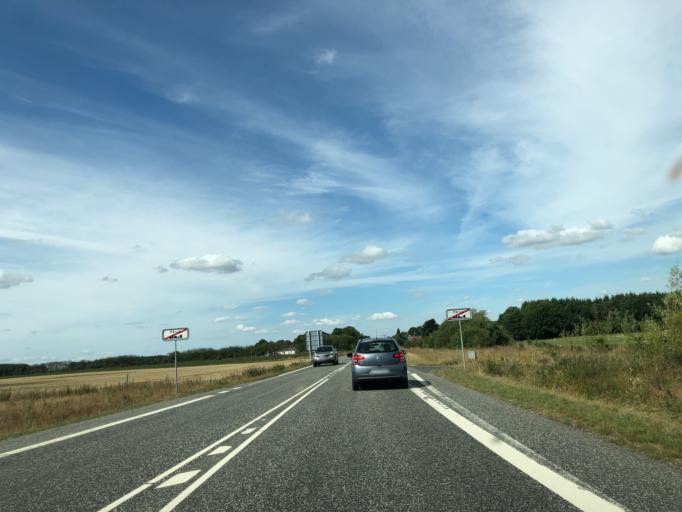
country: DK
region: Central Jutland
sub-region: Ikast-Brande Kommune
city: Bording Kirkeby
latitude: 56.1369
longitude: 9.3419
